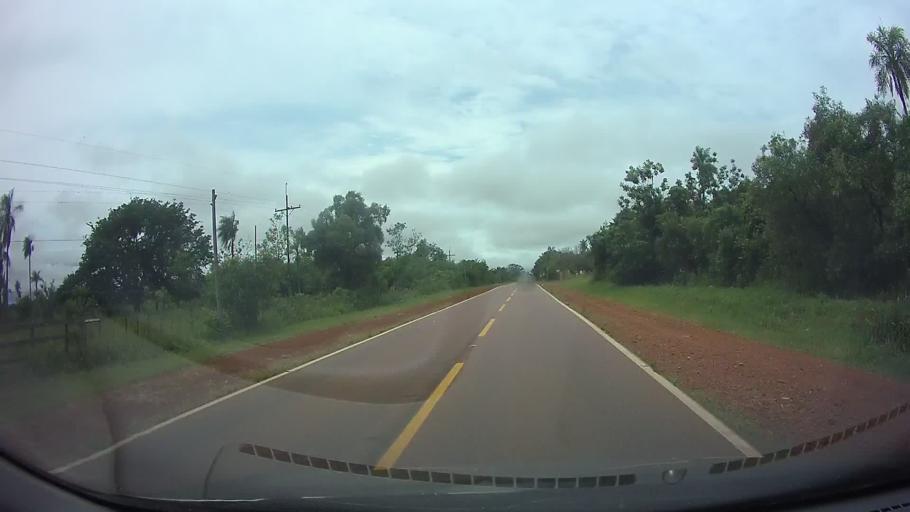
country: PY
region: Paraguari
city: Acahay
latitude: -25.8561
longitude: -57.1371
